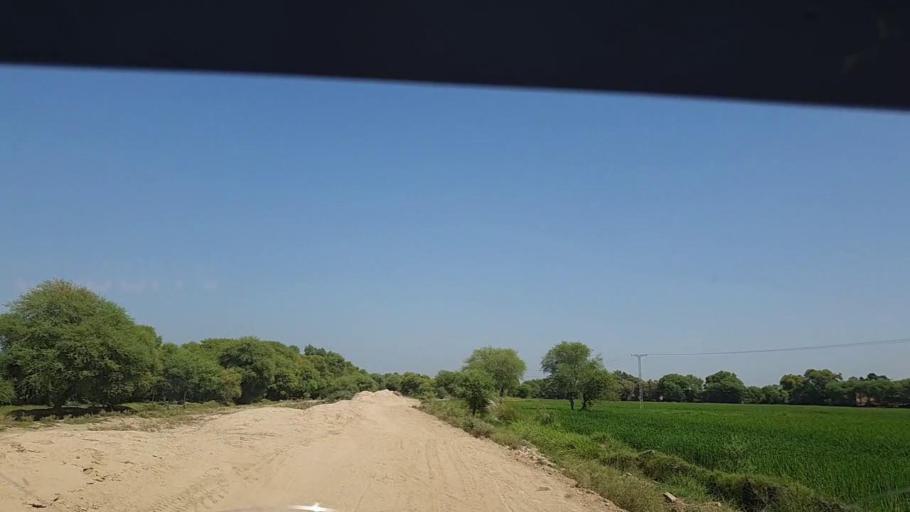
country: PK
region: Sindh
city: Tangwani
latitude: 28.2891
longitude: 69.0542
